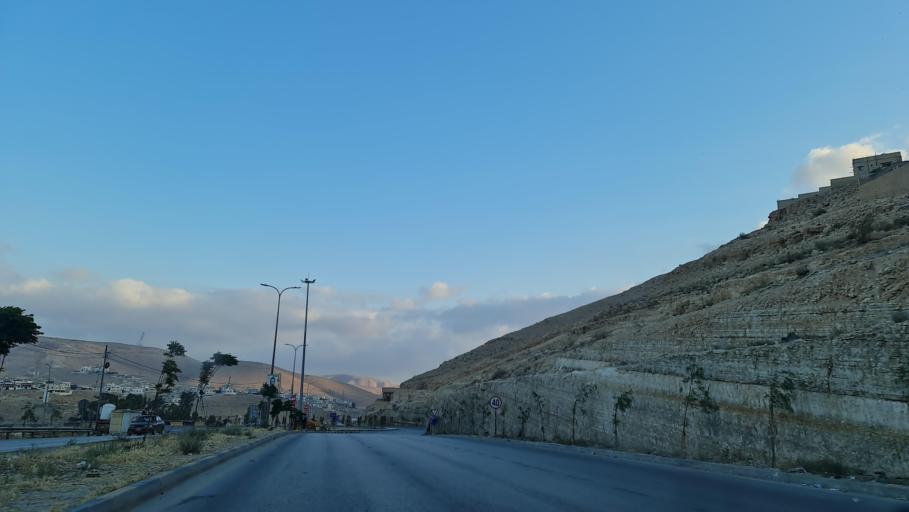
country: JO
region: Zarqa
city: Zarqa
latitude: 32.0807
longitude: 36.0697
